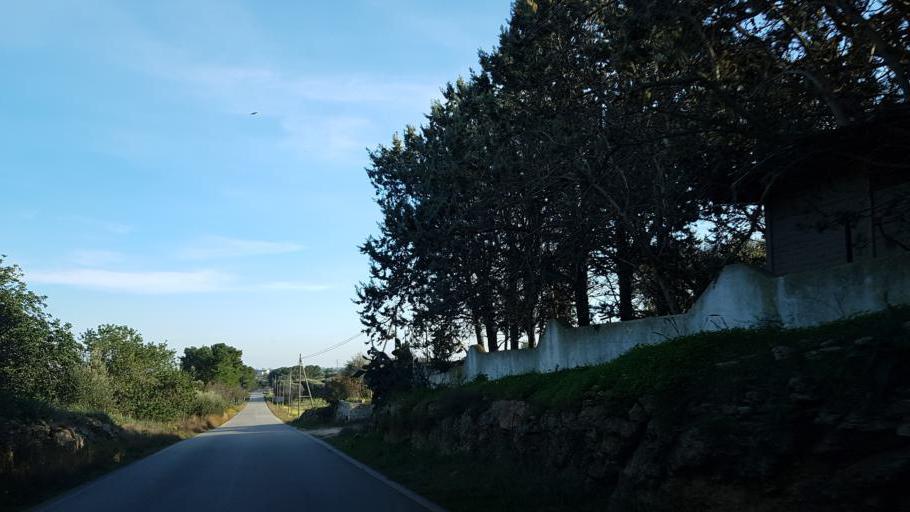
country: IT
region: Apulia
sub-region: Provincia di Brindisi
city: San Vito dei Normanni
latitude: 40.6803
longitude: 17.7720
